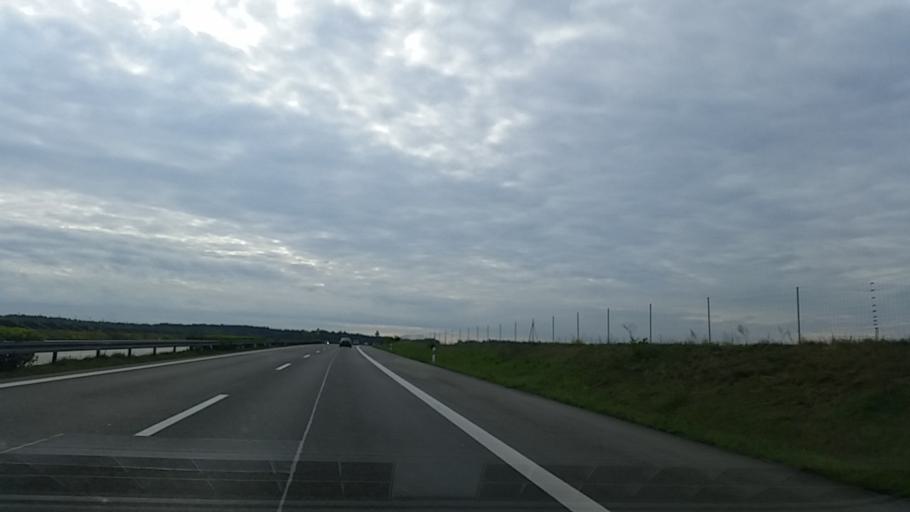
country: DE
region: Brandenburg
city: Heiligengrabe
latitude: 53.1683
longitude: 12.3641
